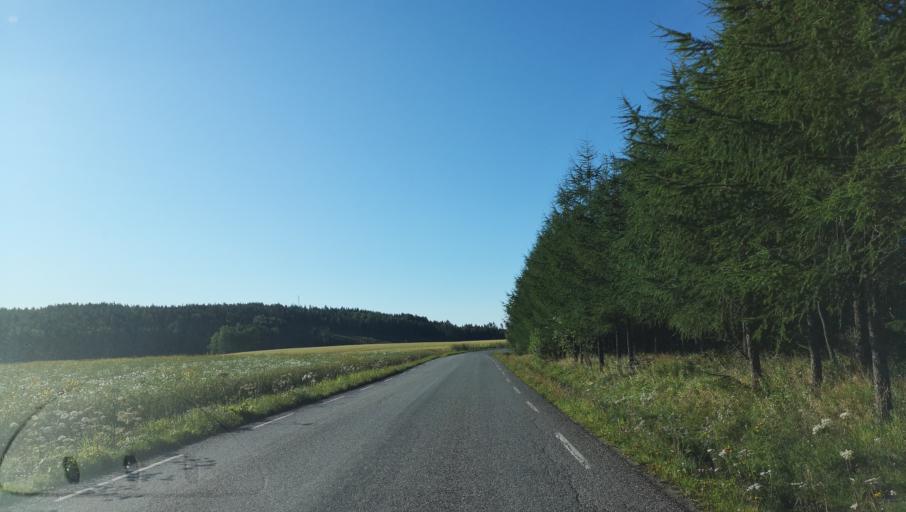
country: NO
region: Ostfold
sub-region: Hobol
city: Knappstad
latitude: 59.6378
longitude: 11.0208
